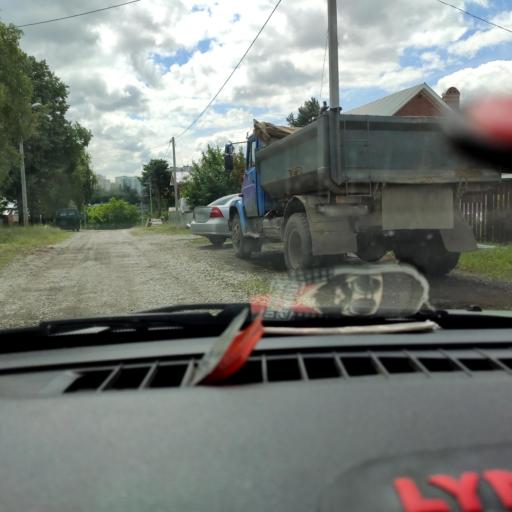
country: RU
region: Perm
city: Perm
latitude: 58.0757
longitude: 56.3579
